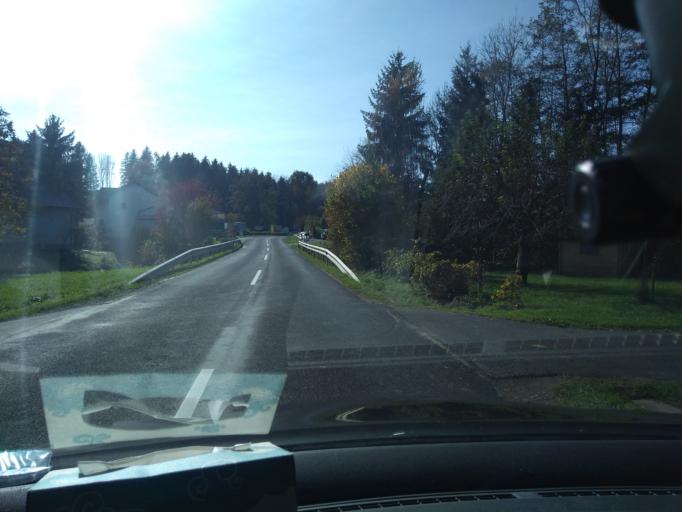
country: AT
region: Styria
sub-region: Politischer Bezirk Leibnitz
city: Allerheiligen bei Wildon
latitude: 46.9098
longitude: 15.5322
